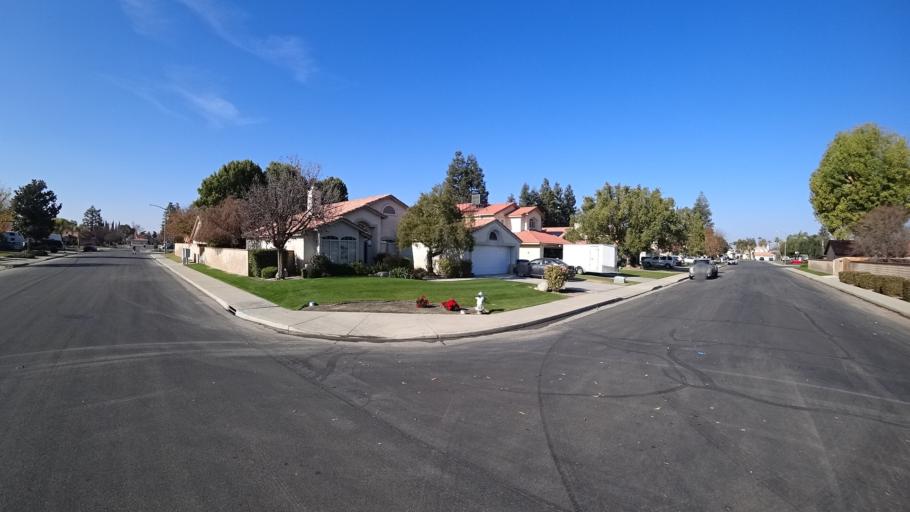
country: US
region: California
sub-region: Kern County
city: Greenacres
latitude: 35.3214
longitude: -119.1152
